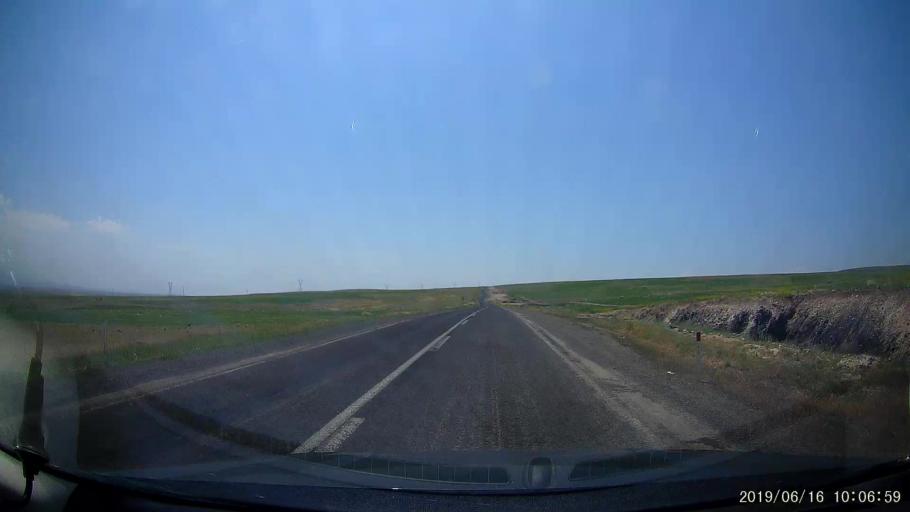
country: TR
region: Kars
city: Digor
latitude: 40.2491
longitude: 43.5496
